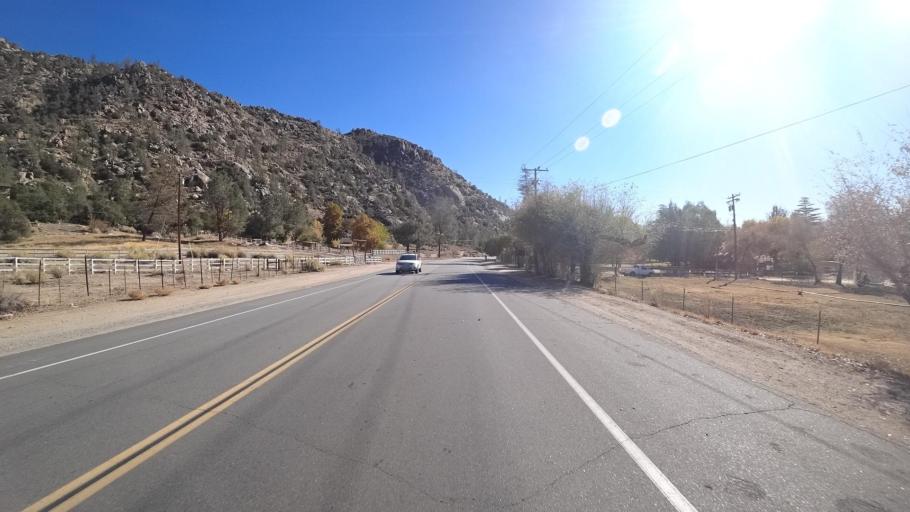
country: US
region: California
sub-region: Kern County
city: Kernville
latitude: 35.7510
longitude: -118.4144
